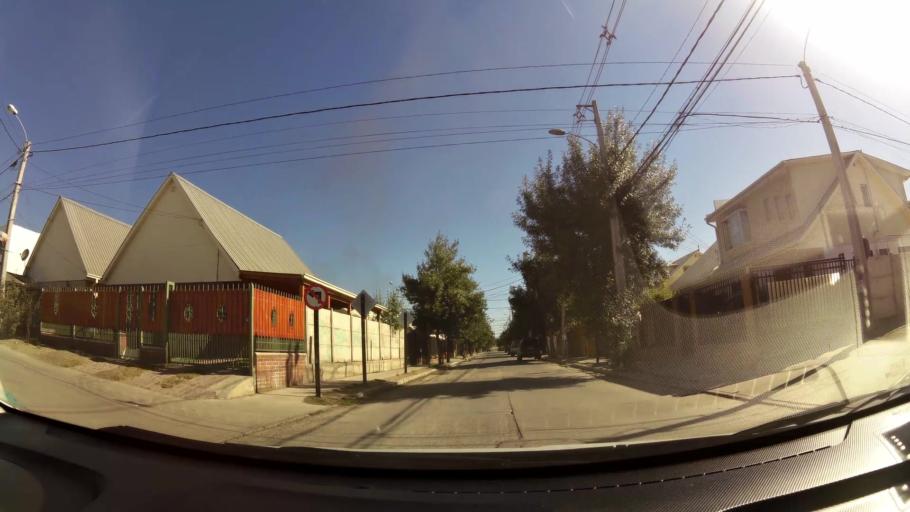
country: CL
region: O'Higgins
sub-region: Provincia de Cachapoal
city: Rancagua
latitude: -34.1819
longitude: -70.7727
